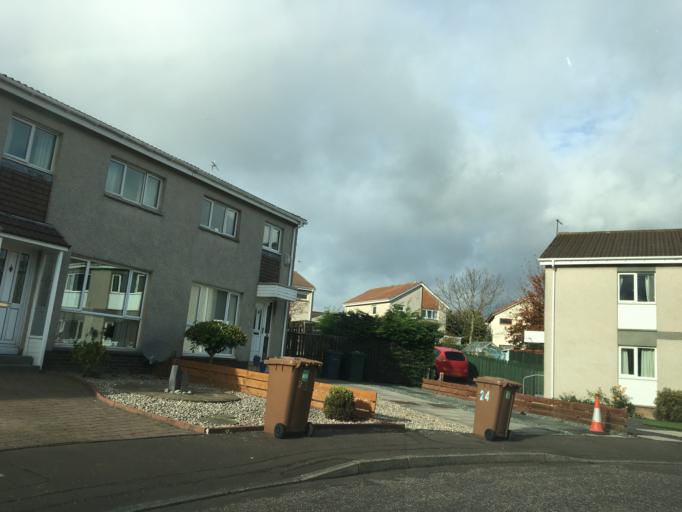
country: GB
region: Scotland
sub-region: Midlothian
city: Loanhead
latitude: 55.9042
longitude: -3.1678
